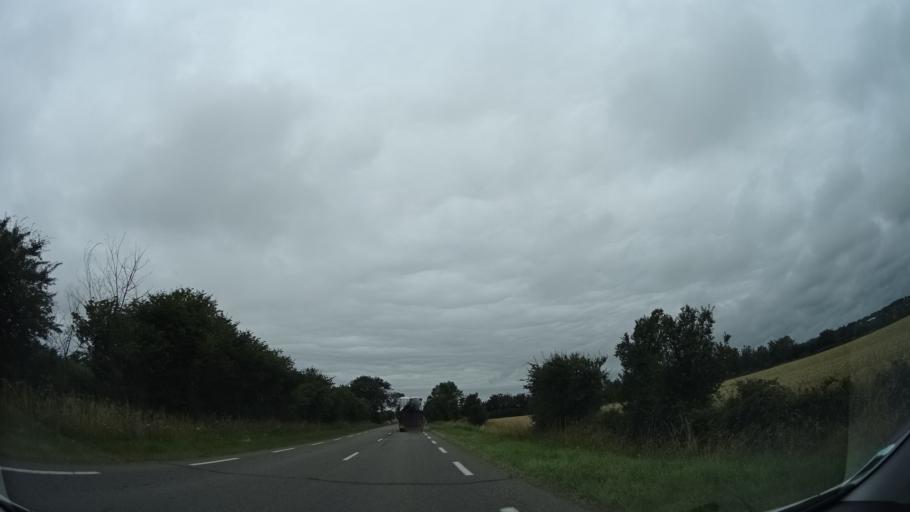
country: FR
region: Lower Normandy
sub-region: Departement de la Manche
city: Portbail
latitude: 49.3633
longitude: -1.7059
